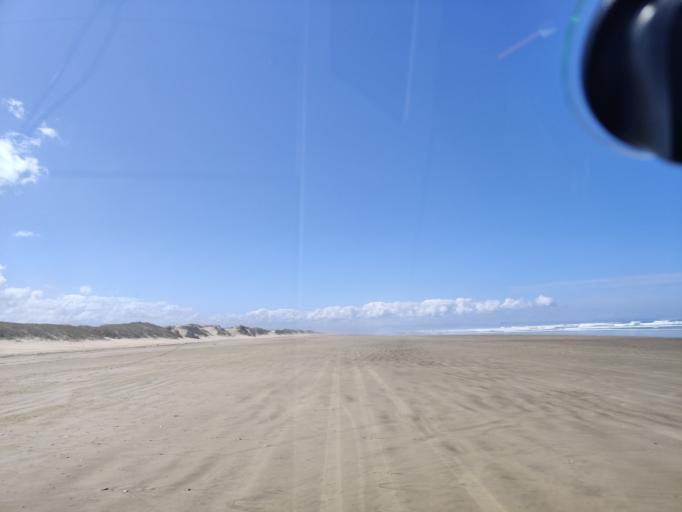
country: NZ
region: Northland
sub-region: Far North District
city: Ahipara
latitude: -34.9069
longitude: 173.0901
